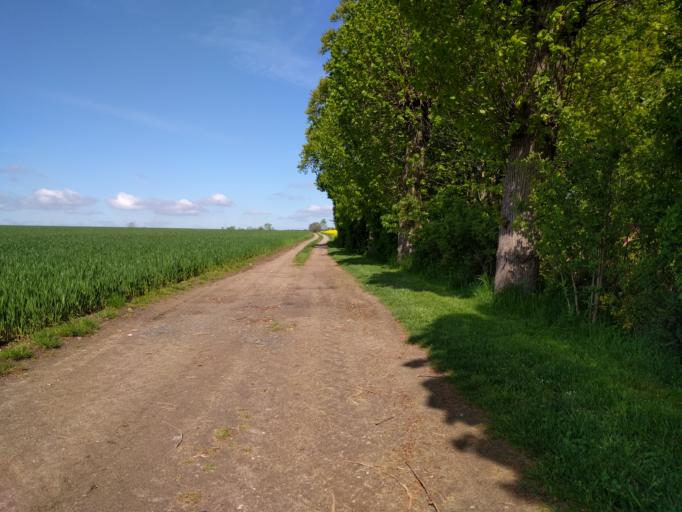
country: DK
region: South Denmark
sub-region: Kerteminde Kommune
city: Langeskov
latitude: 55.3820
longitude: 10.5612
